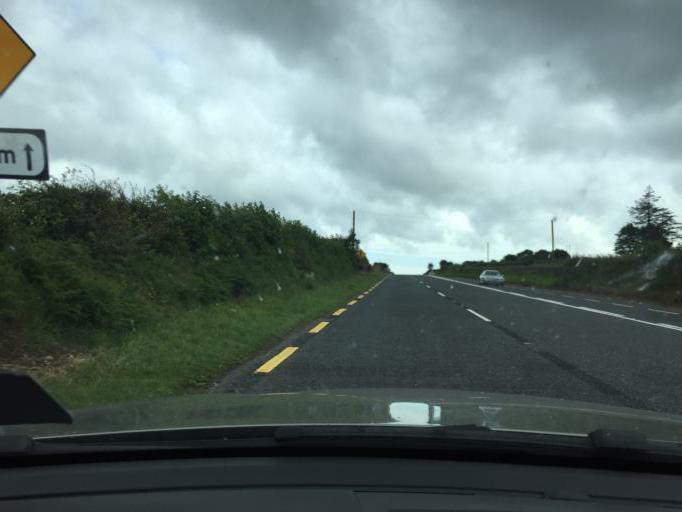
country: IE
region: Munster
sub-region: Waterford
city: Dungarvan
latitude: 52.1294
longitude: -7.5633
